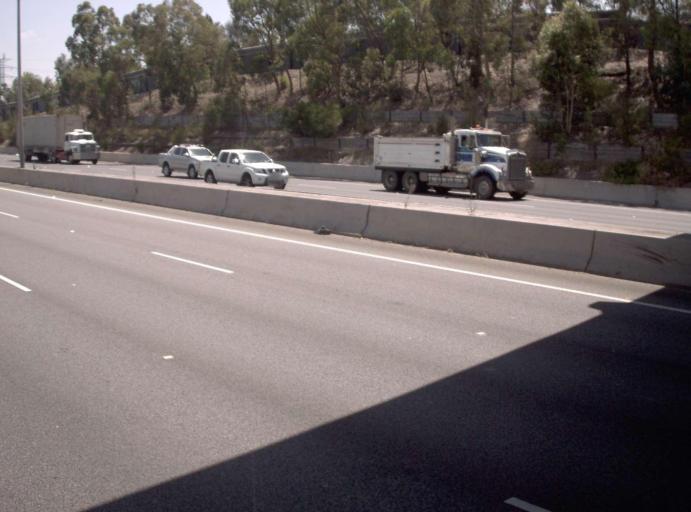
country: AU
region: Victoria
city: Carnegie
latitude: -37.8734
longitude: 145.0657
